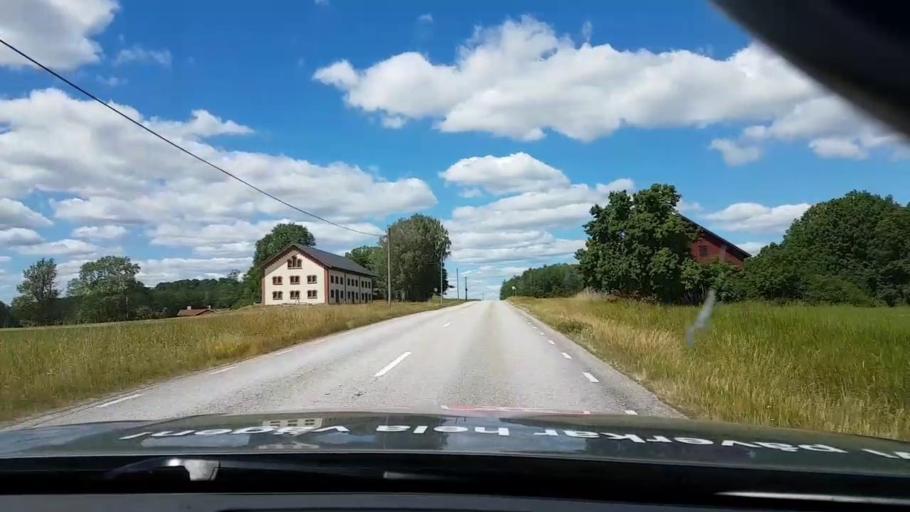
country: SE
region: Kalmar
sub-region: Vasterviks Kommun
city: Forserum
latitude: 58.0458
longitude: 16.4153
